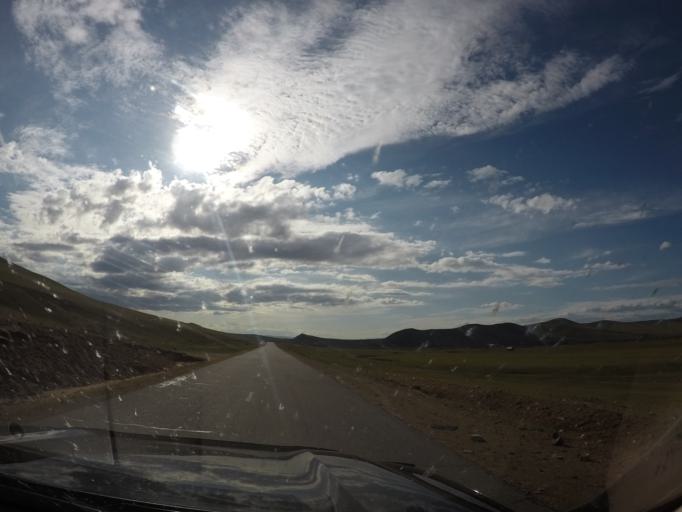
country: MN
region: Central Aimak
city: Bayandelger
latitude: 47.6936
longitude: 108.4936
